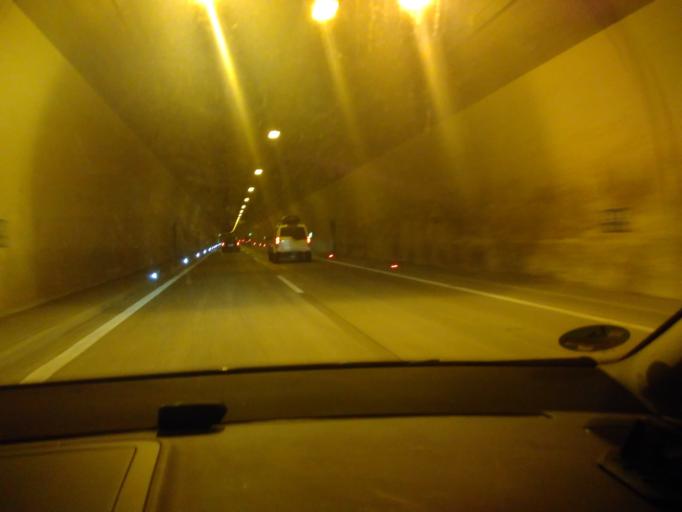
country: AT
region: Salzburg
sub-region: Politischer Bezirk Hallein
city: Golling an der Salzach
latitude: 47.5675
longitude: 13.1712
